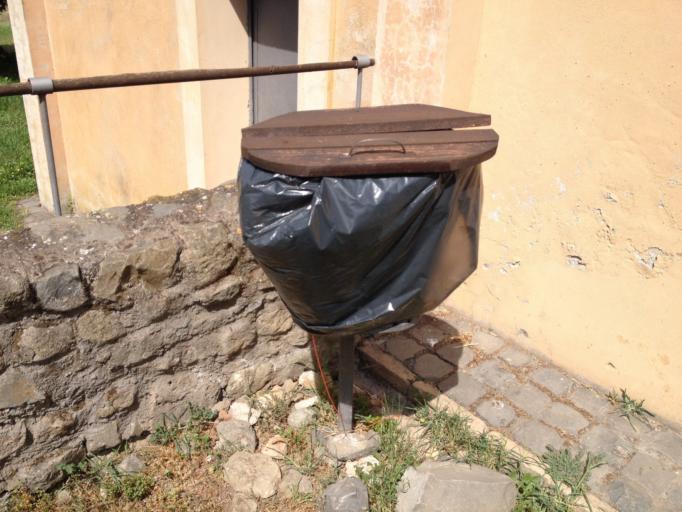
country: IT
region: Latium
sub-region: Citta metropolitana di Roma Capitale
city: Ciampino
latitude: 41.8313
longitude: 12.5541
